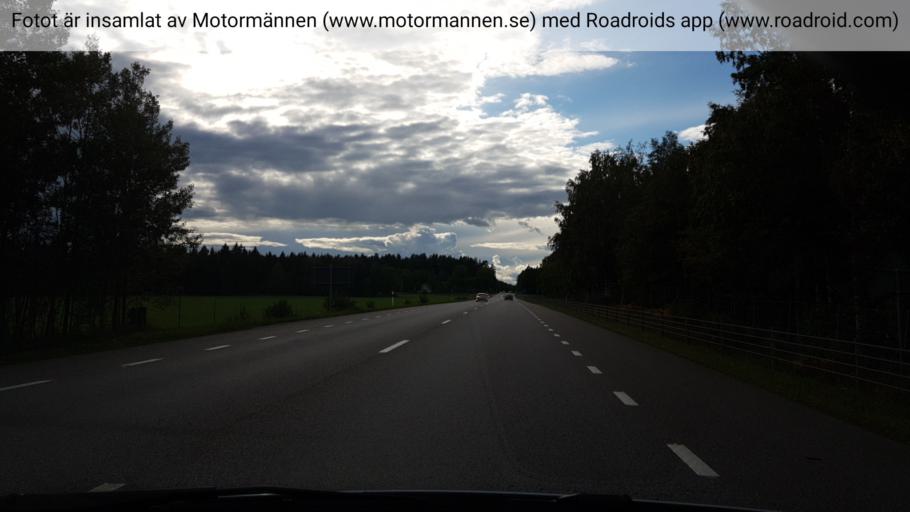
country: SE
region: Vaestra Goetaland
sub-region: Tibro Kommun
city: Tibro
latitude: 58.4153
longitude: 14.0747
